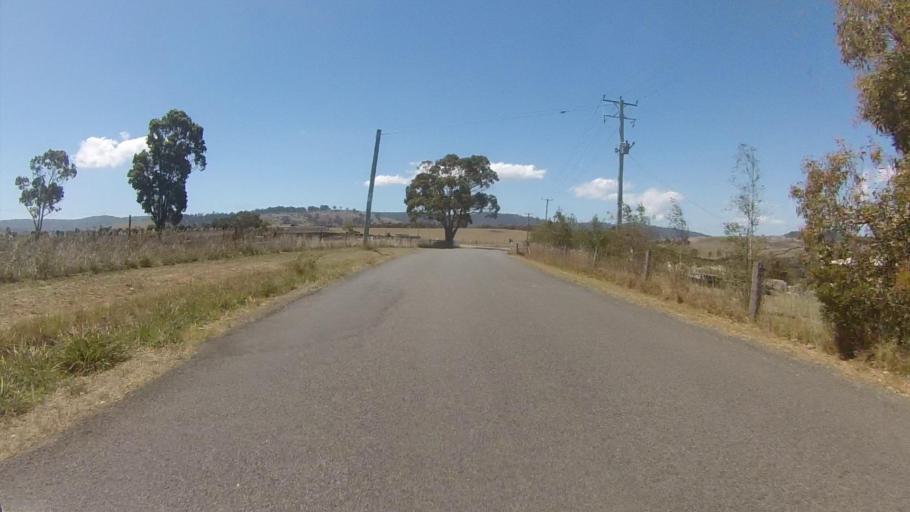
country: AU
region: Tasmania
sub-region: Sorell
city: Sorell
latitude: -42.7740
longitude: 147.5818
